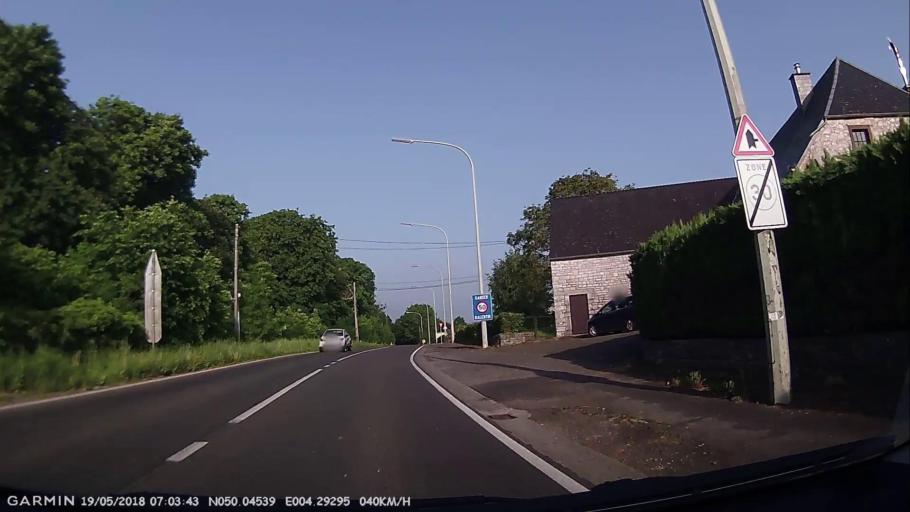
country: BE
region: Wallonia
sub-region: Province du Hainaut
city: Chimay
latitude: 50.0454
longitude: 4.2929
